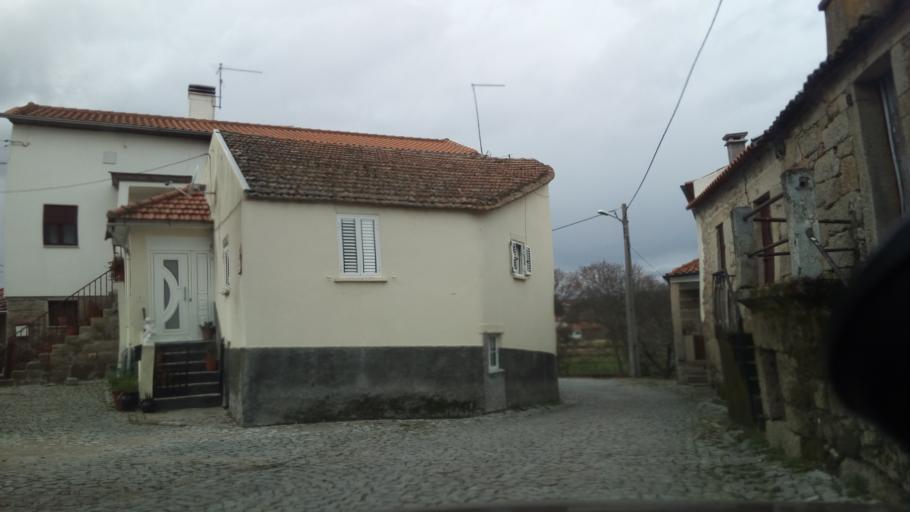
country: PT
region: Guarda
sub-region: Fornos de Algodres
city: Fornos de Algodres
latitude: 40.5810
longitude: -7.4733
